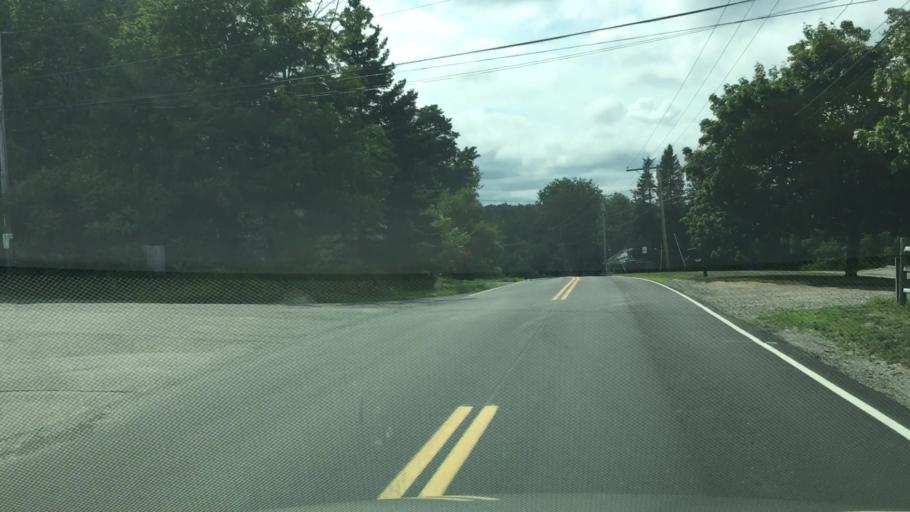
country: US
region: Maine
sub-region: Penobscot County
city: Hampden
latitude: 44.7318
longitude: -68.8609
